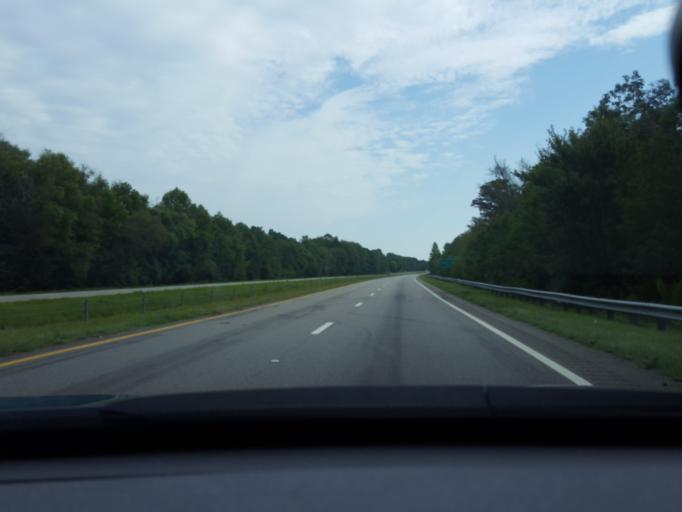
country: US
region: North Carolina
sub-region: Chowan County
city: Edenton
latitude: 36.0663
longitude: -76.6457
